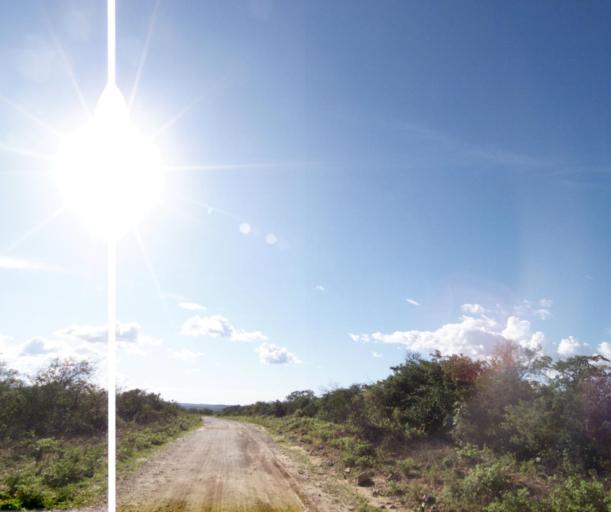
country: BR
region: Bahia
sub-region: Tanhacu
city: Tanhacu
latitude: -14.1886
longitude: -40.9768
